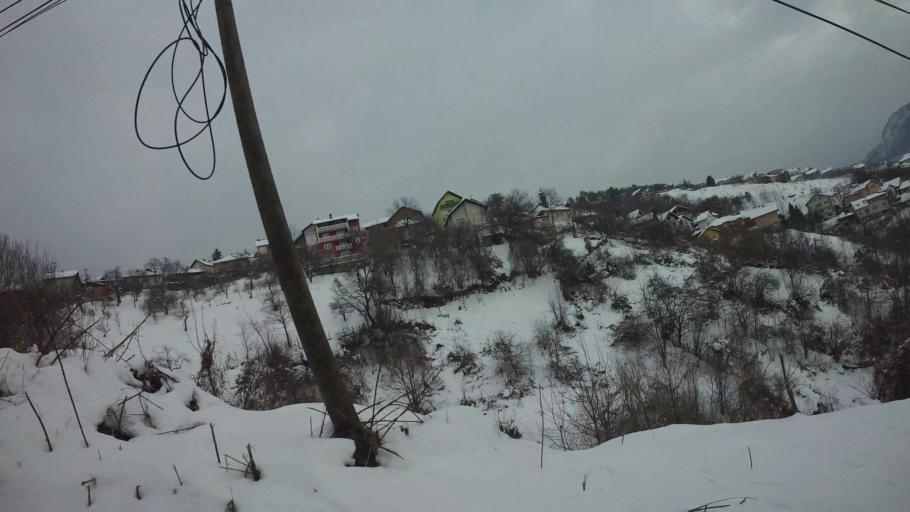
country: BA
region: Federation of Bosnia and Herzegovina
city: Kobilja Glava
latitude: 43.8681
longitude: 18.4354
